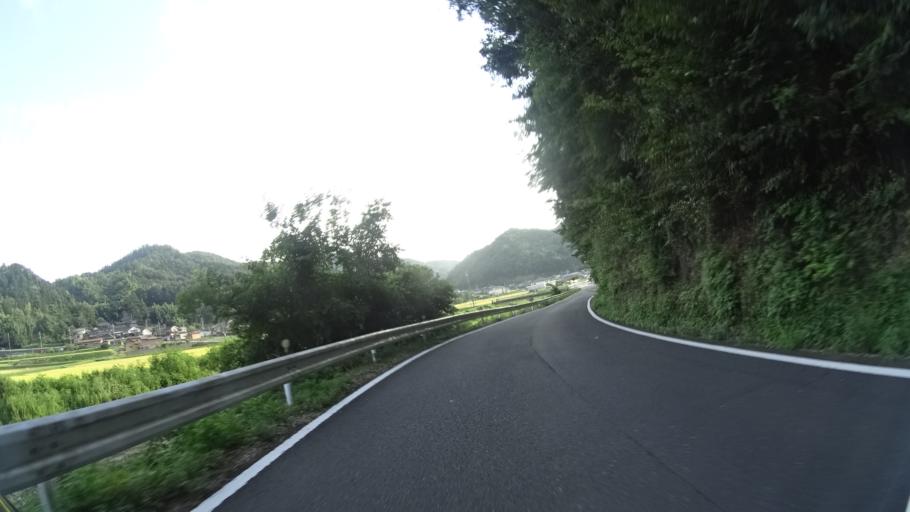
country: JP
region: Kyoto
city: Maizuru
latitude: 35.4112
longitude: 135.3475
